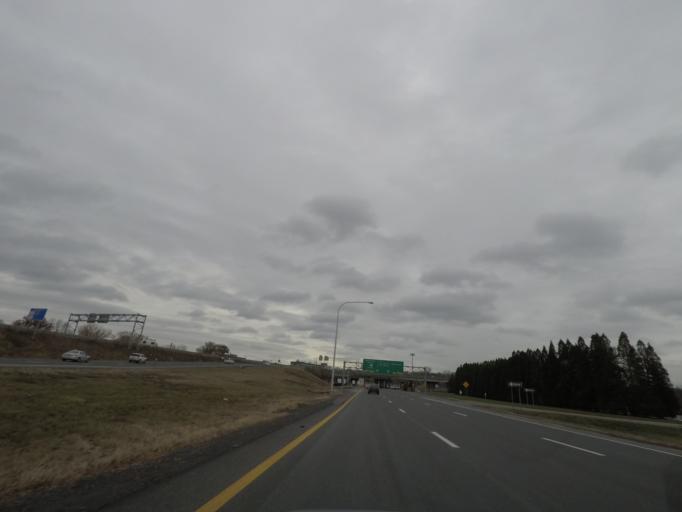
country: US
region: New York
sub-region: Schenectady County
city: Schenectady
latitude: 42.8123
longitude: -73.9536
